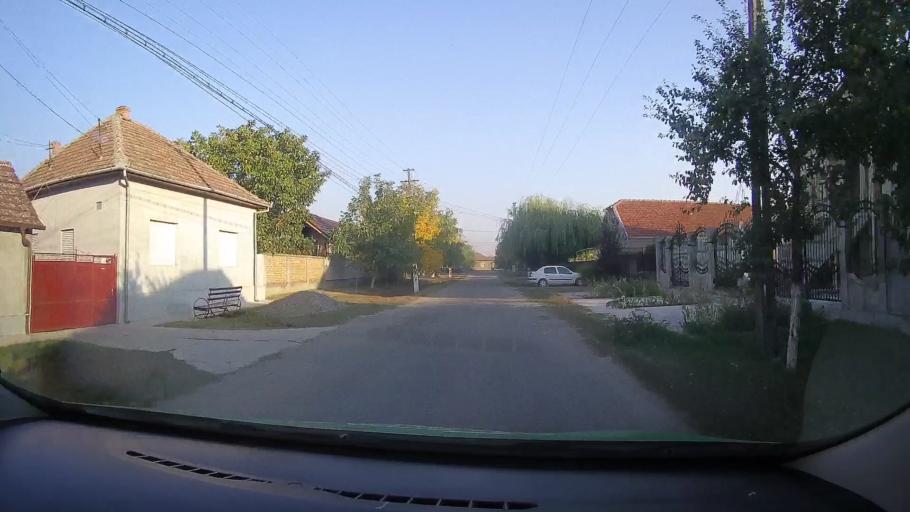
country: RO
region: Arad
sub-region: Comuna Curtici
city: Curtici
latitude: 46.3420
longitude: 21.3119
